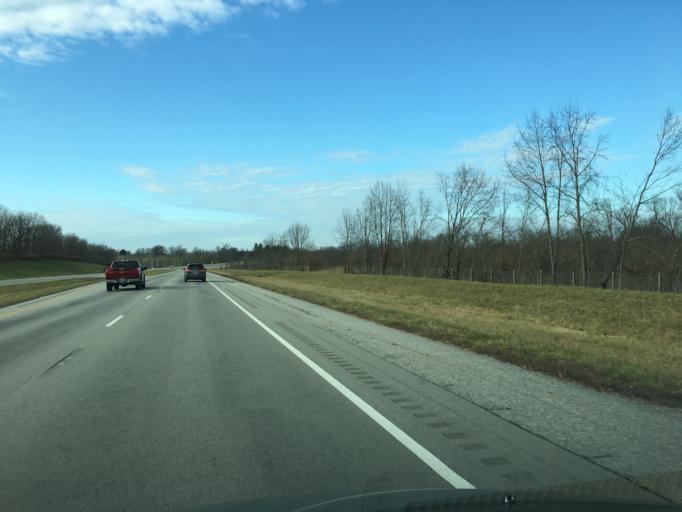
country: US
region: Kentucky
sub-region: Scott County
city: Georgetown
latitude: 38.2026
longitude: -84.5913
